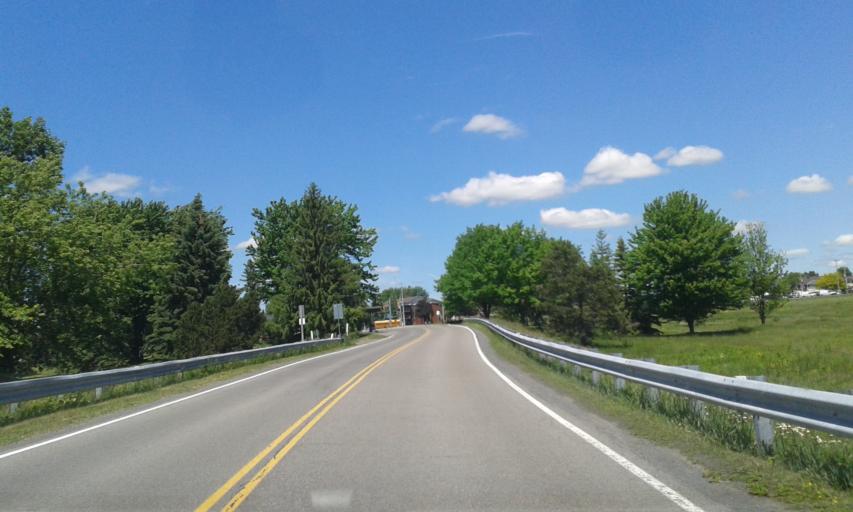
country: US
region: New York
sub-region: St. Lawrence County
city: Massena
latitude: 45.0253
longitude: -74.8958
